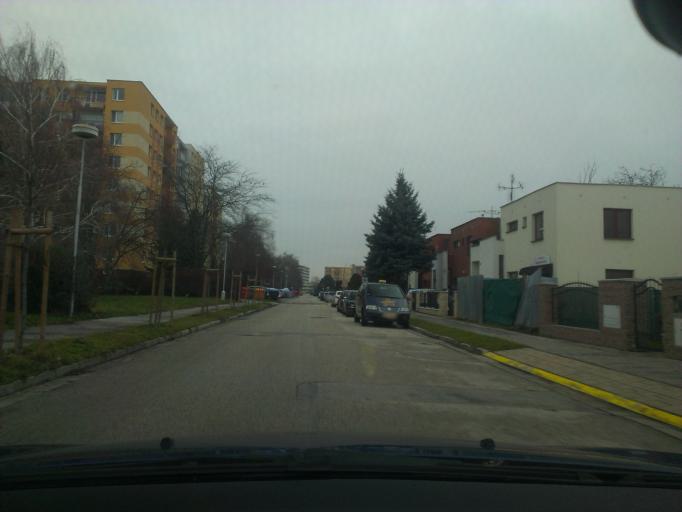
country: SK
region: Trnavsky
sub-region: Okres Trnava
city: Piestany
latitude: 48.5822
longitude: 17.8201
